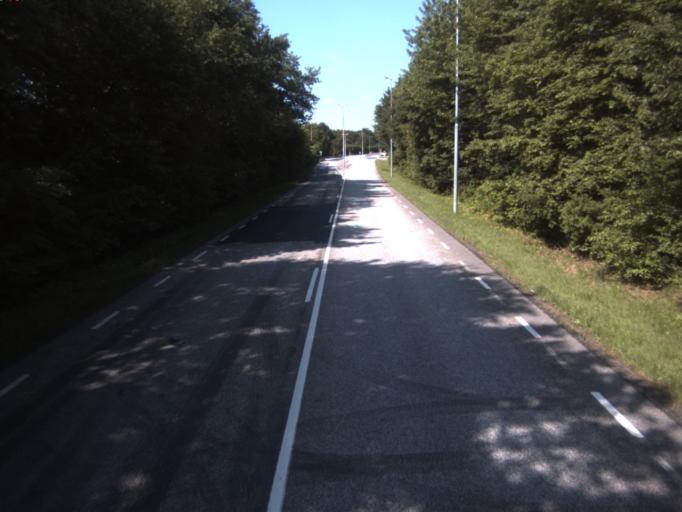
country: SE
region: Skane
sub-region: Helsingborg
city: Helsingborg
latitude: 56.0260
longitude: 12.7469
